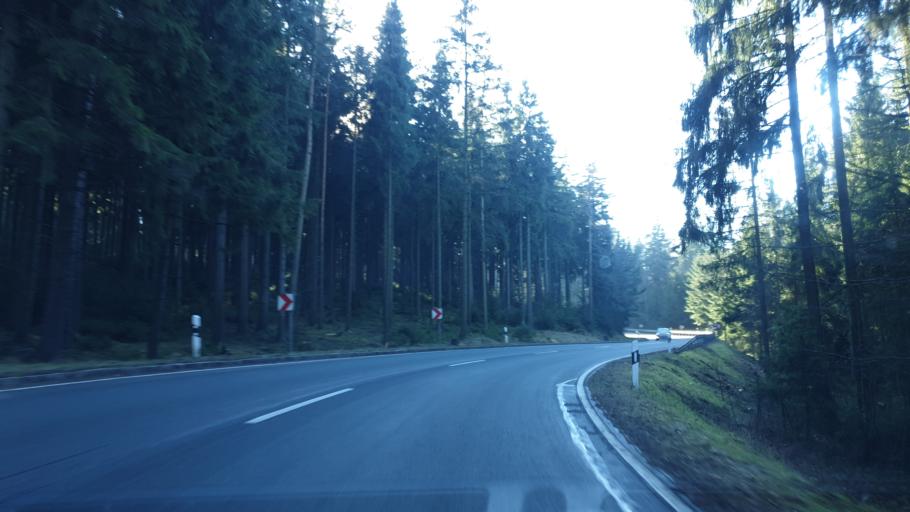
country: DE
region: Saxony
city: Bad Brambach
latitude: 50.2039
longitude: 12.3152
